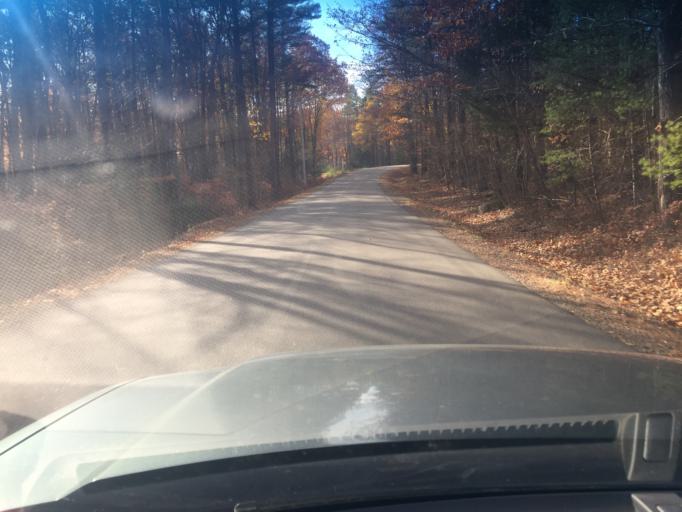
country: US
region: Maine
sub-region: York County
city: Eliot
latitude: 43.1911
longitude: -70.7482
